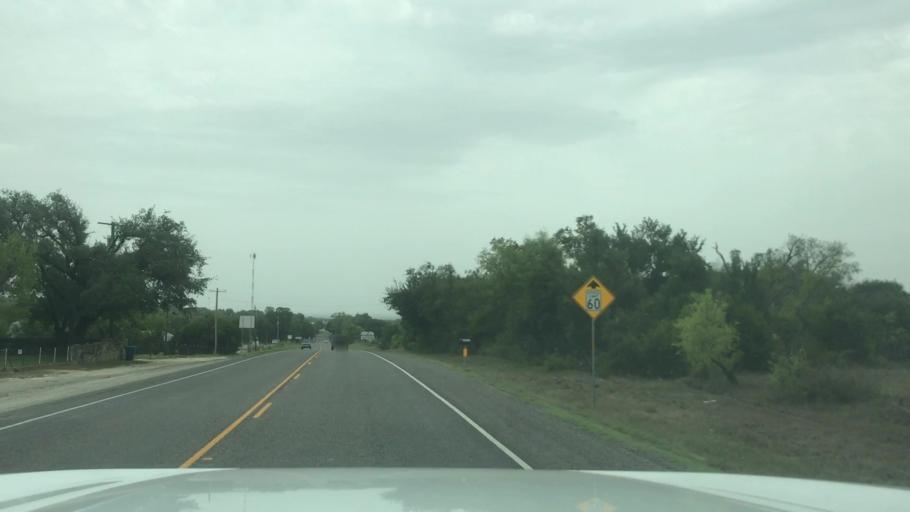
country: US
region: Texas
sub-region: Hamilton County
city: Hico
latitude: 31.9938
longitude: -98.0445
